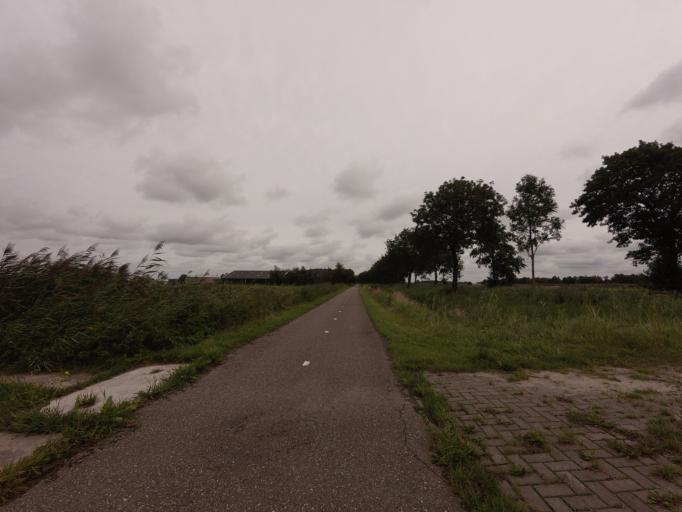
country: NL
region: Overijssel
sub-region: Gemeente Steenwijkerland
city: Oldemarkt
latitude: 52.7997
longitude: 5.8997
